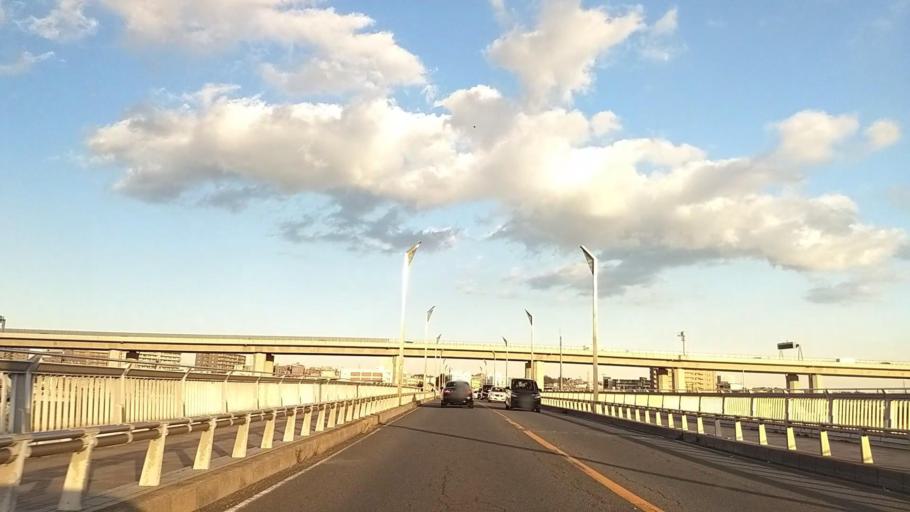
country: JP
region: Kanagawa
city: Atsugi
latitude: 35.4441
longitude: 139.3728
